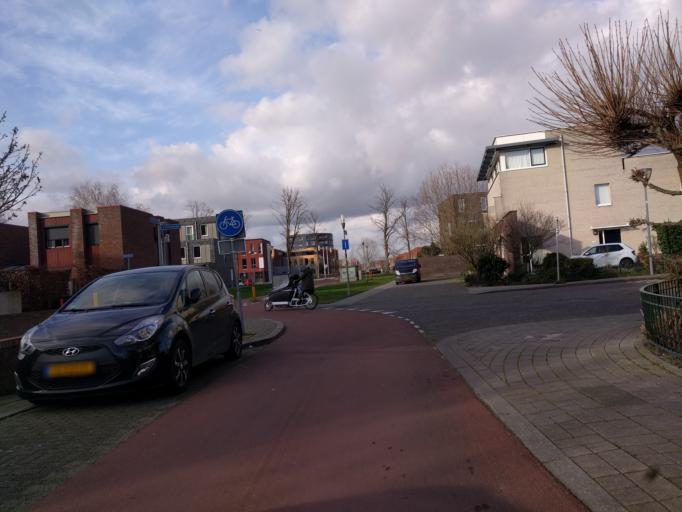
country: NL
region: Gelderland
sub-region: Gemeente Nijmegen
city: Nijmegen
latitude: 51.8691
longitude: 5.8694
